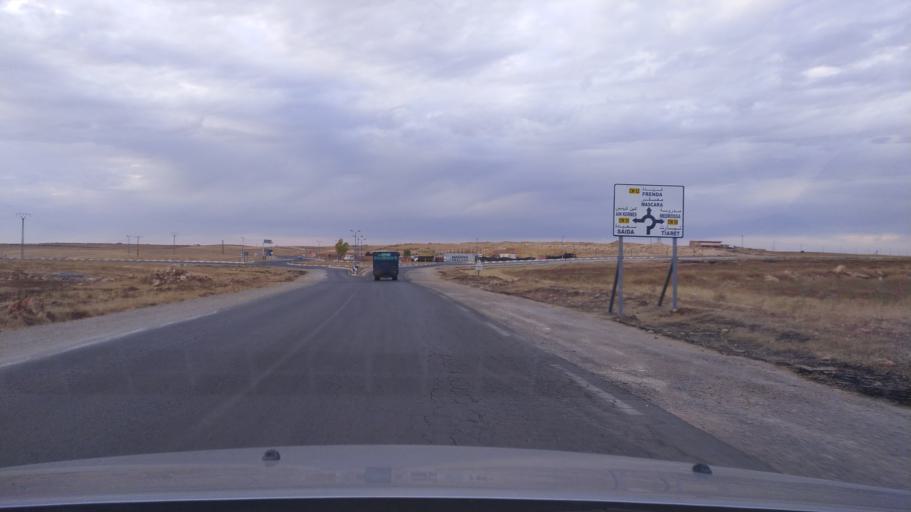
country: DZ
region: Tiaret
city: Frenda
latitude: 34.9905
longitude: 1.1308
